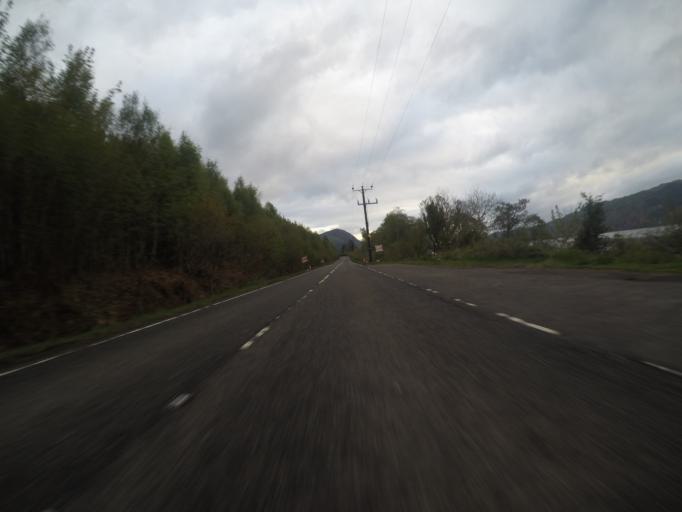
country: GB
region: Scotland
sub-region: Highland
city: Beauly
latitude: 57.1933
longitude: -4.6149
